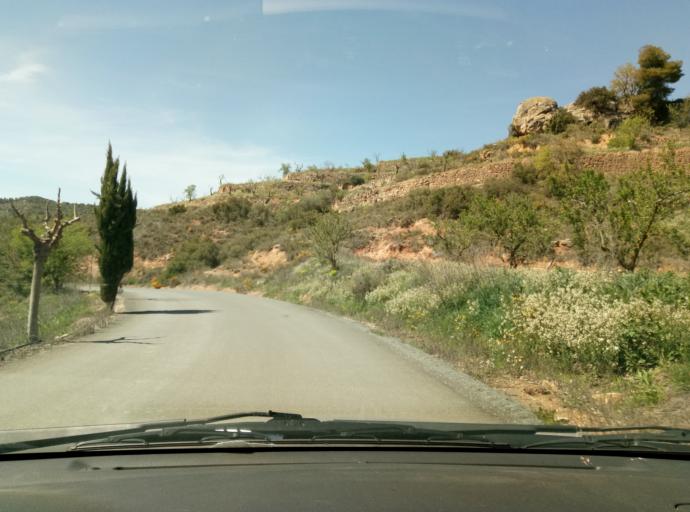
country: ES
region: Catalonia
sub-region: Provincia de Lleida
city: Juncosa
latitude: 41.4254
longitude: 0.8572
